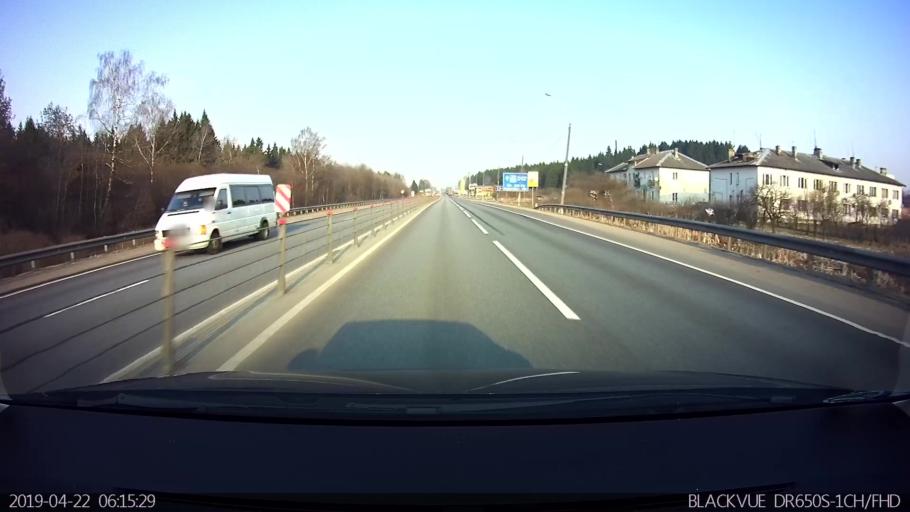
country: RU
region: Moskovskaya
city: Mozhaysk
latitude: 55.4587
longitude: 36.0443
